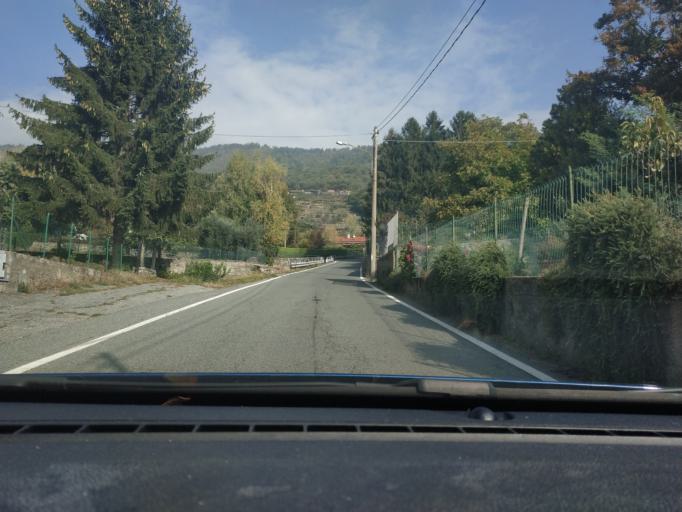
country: IT
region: Piedmont
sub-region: Provincia di Torino
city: Chiaverano
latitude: 45.5021
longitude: 7.9079
